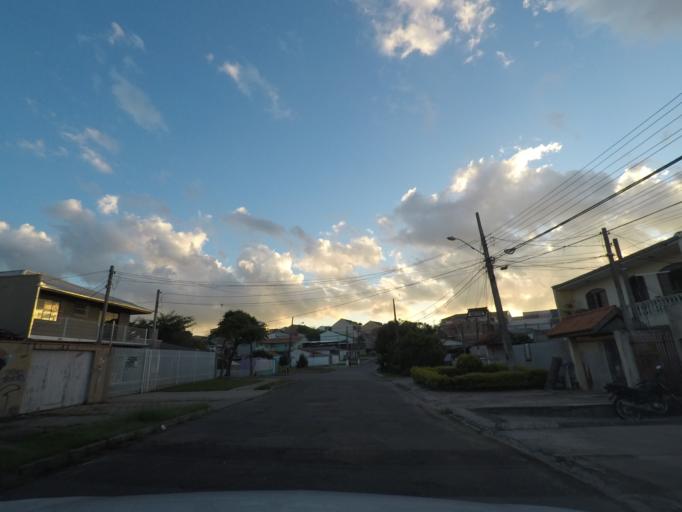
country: BR
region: Parana
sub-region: Sao Jose Dos Pinhais
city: Sao Jose dos Pinhais
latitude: -25.5007
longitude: -49.2585
